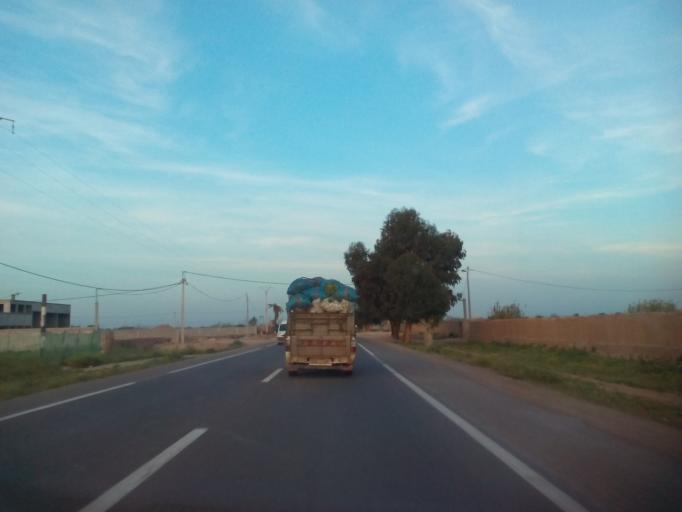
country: MA
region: Marrakech-Tensift-Al Haouz
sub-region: Marrakech
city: Marrakesh
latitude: 31.6260
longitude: -8.2786
